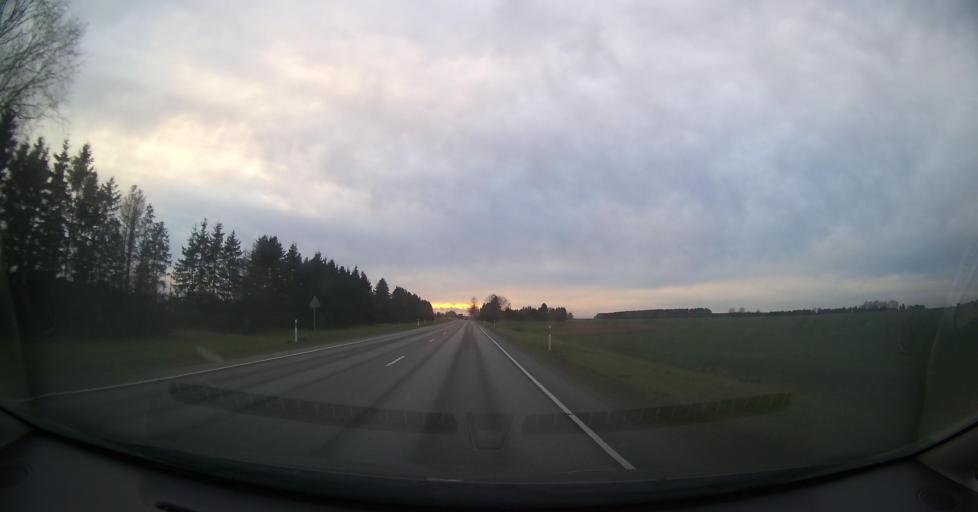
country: EE
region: Ida-Virumaa
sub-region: Kohtla-Nomme vald
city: Kohtla-Nomme
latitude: 59.4182
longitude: 27.1564
